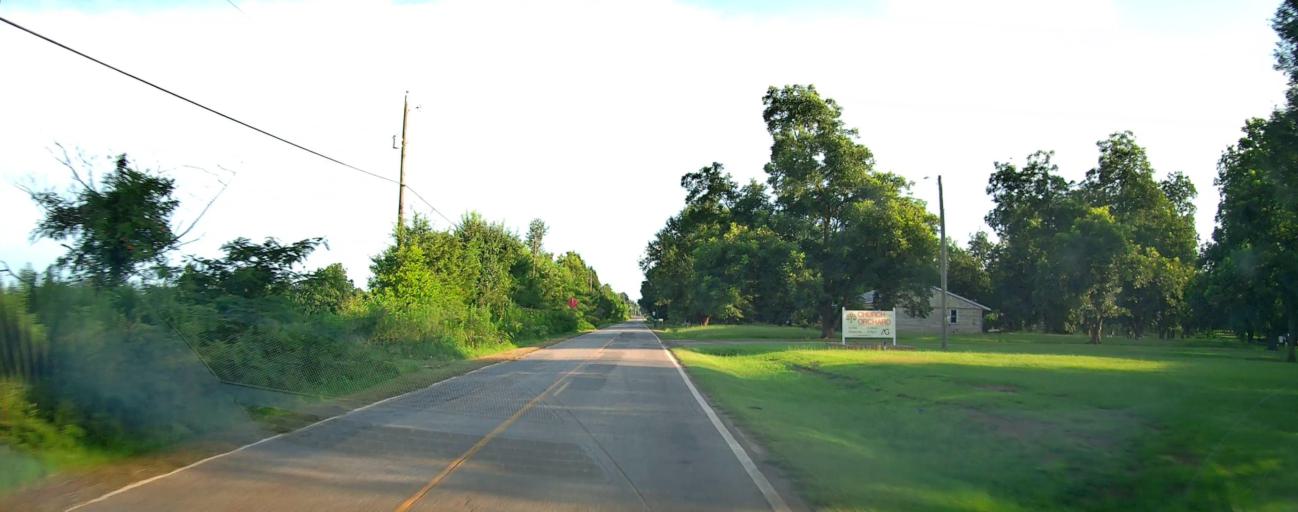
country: US
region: Georgia
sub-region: Peach County
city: Fort Valley
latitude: 32.5768
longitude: -83.8738
